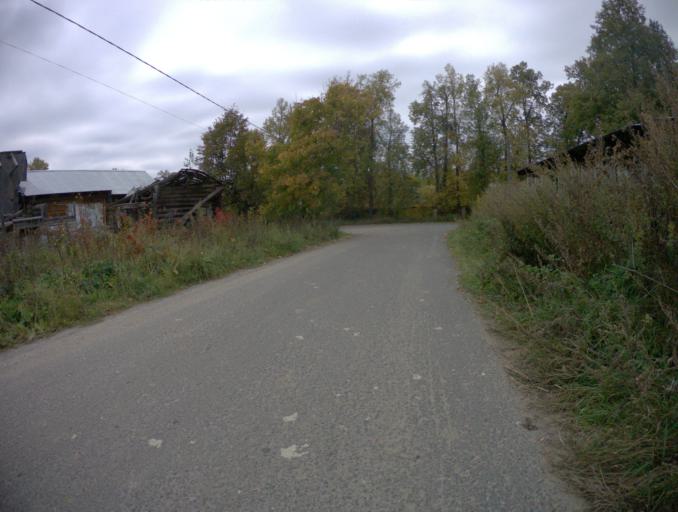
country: RU
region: Vladimir
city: Mstera
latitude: 56.3904
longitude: 41.9158
